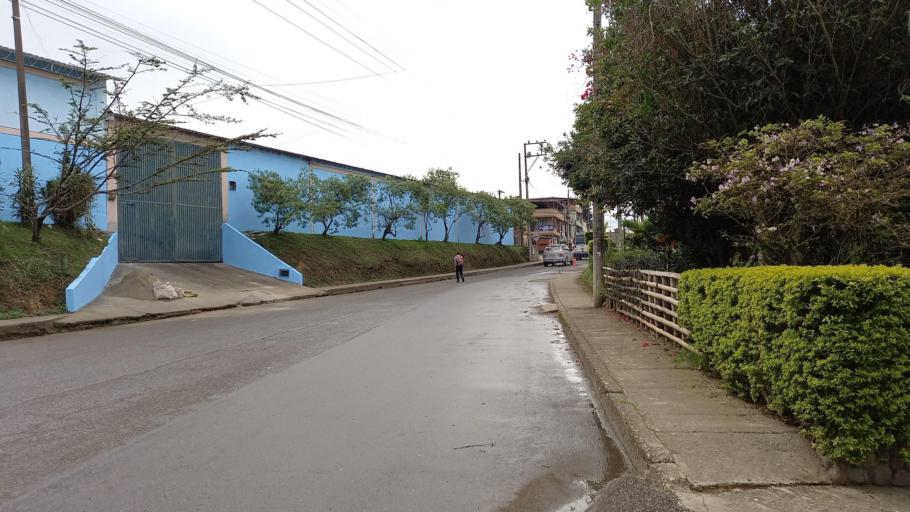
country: CO
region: Cauca
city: Popayan
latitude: 2.4583
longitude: -76.6436
